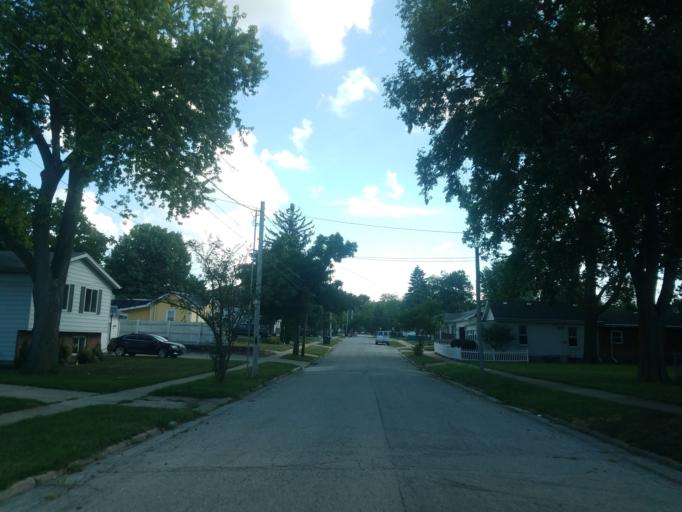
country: US
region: Illinois
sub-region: McLean County
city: Bloomington
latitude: 40.4706
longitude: -88.9911
